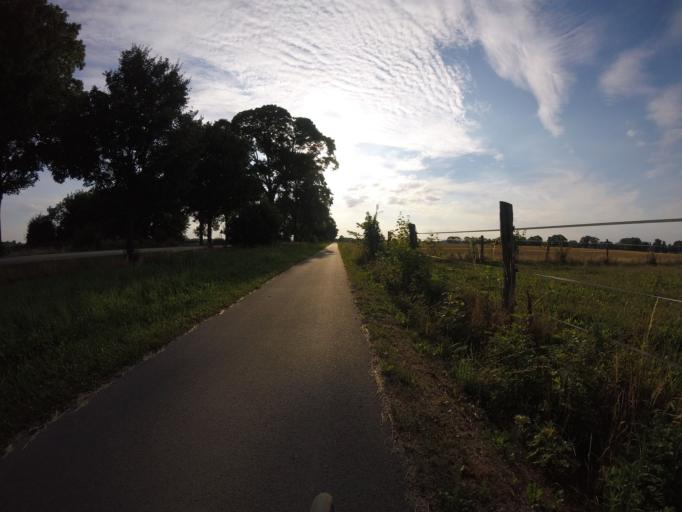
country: DE
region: Brandenburg
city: Altlandsberg
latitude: 52.5642
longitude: 13.7500
